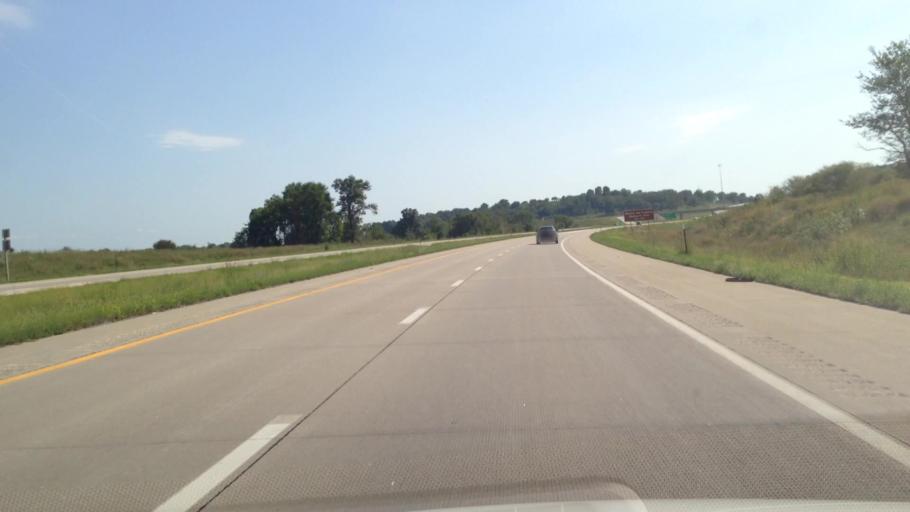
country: US
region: Kansas
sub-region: Linn County
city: Pleasanton
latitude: 38.2702
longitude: -94.6686
